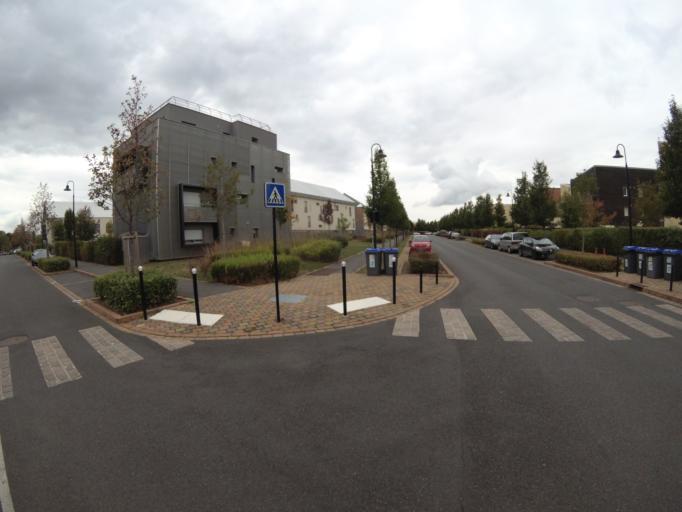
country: FR
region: Ile-de-France
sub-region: Departement de Seine-et-Marne
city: Chessy
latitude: 48.8786
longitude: 2.7728
